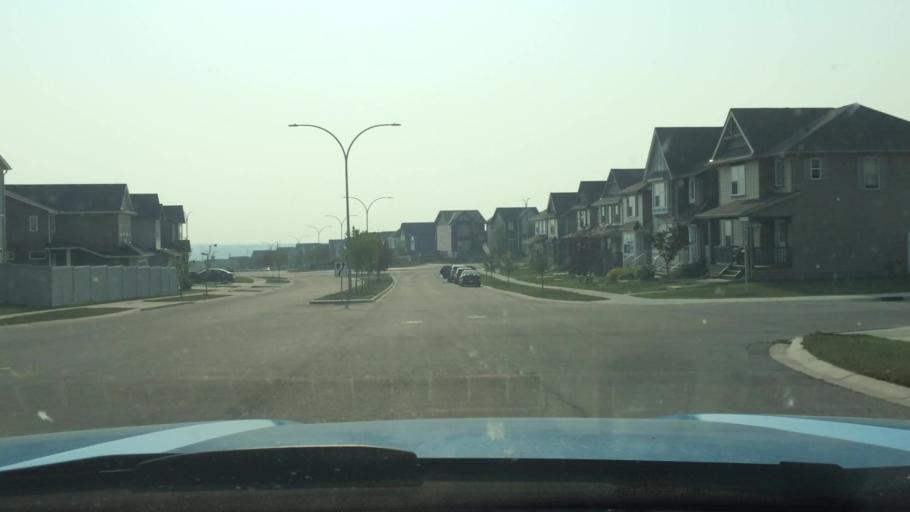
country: CA
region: Alberta
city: Calgary
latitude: 51.1800
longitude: -114.1559
